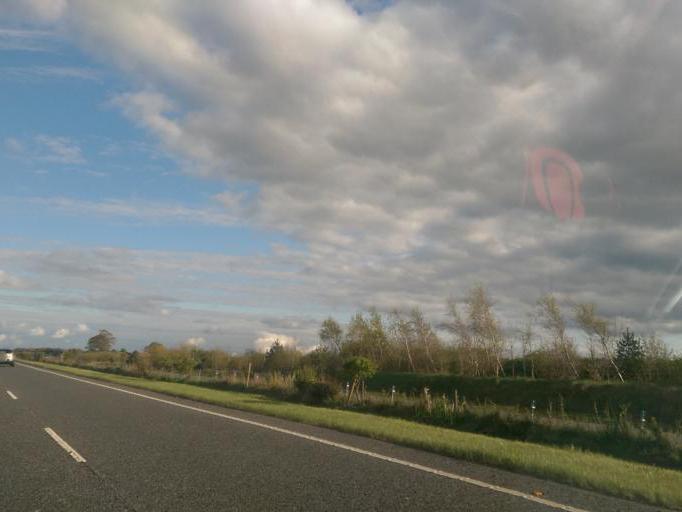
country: IE
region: Leinster
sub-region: An Mhi
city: Longwood
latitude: 53.4334
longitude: -6.9977
